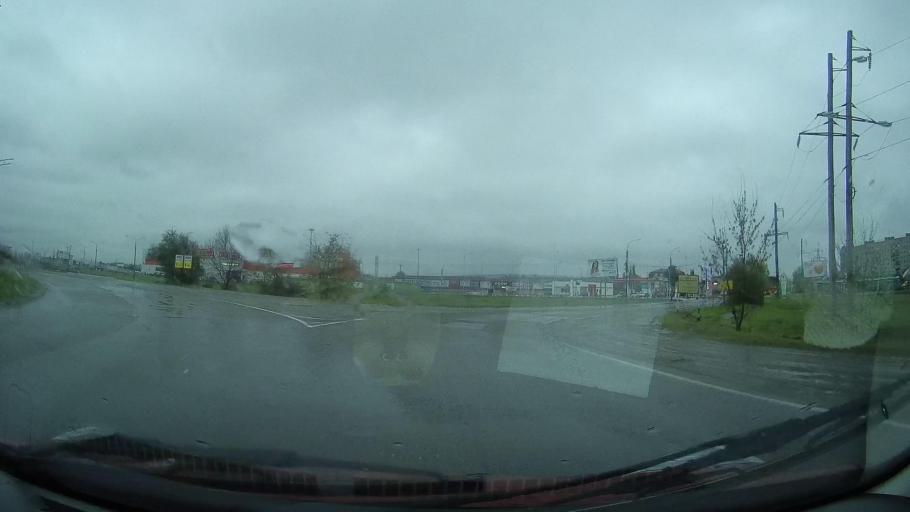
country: RU
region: Stavropol'skiy
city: Nevinnomyssk
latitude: 44.6419
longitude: 41.9594
